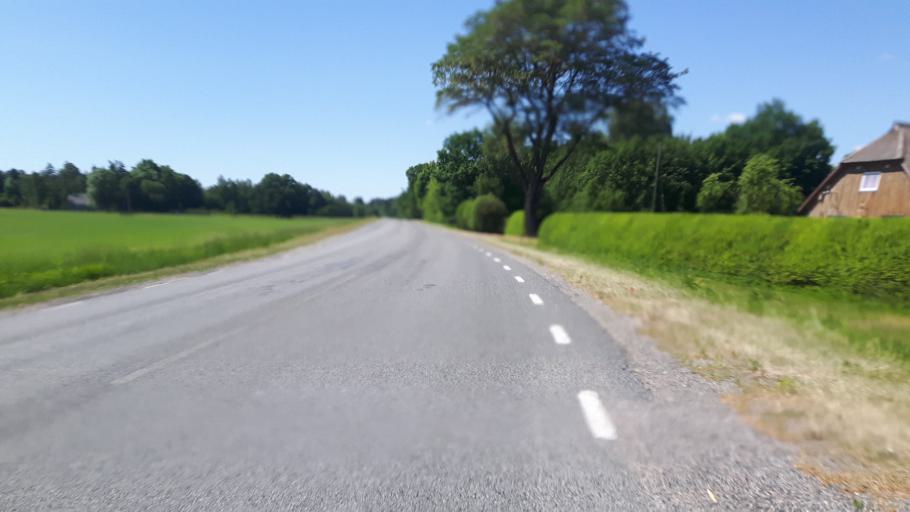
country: EE
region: Paernumaa
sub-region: Tootsi vald
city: Tootsi
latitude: 58.4981
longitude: 24.8722
